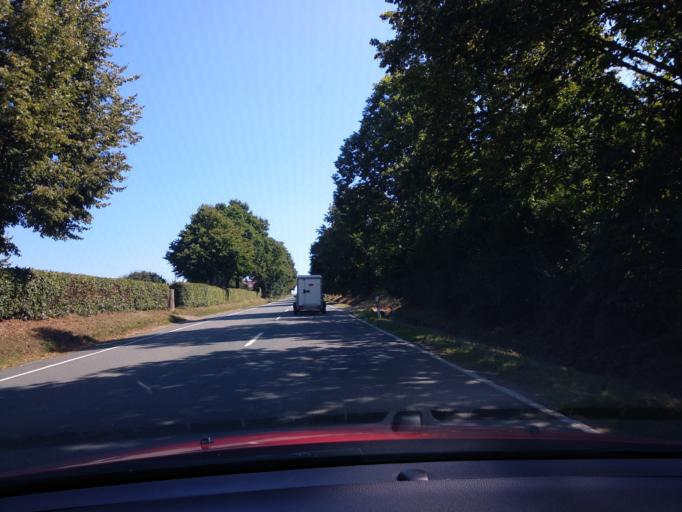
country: DE
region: North Rhine-Westphalia
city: Brakel
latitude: 51.6535
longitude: 9.1268
